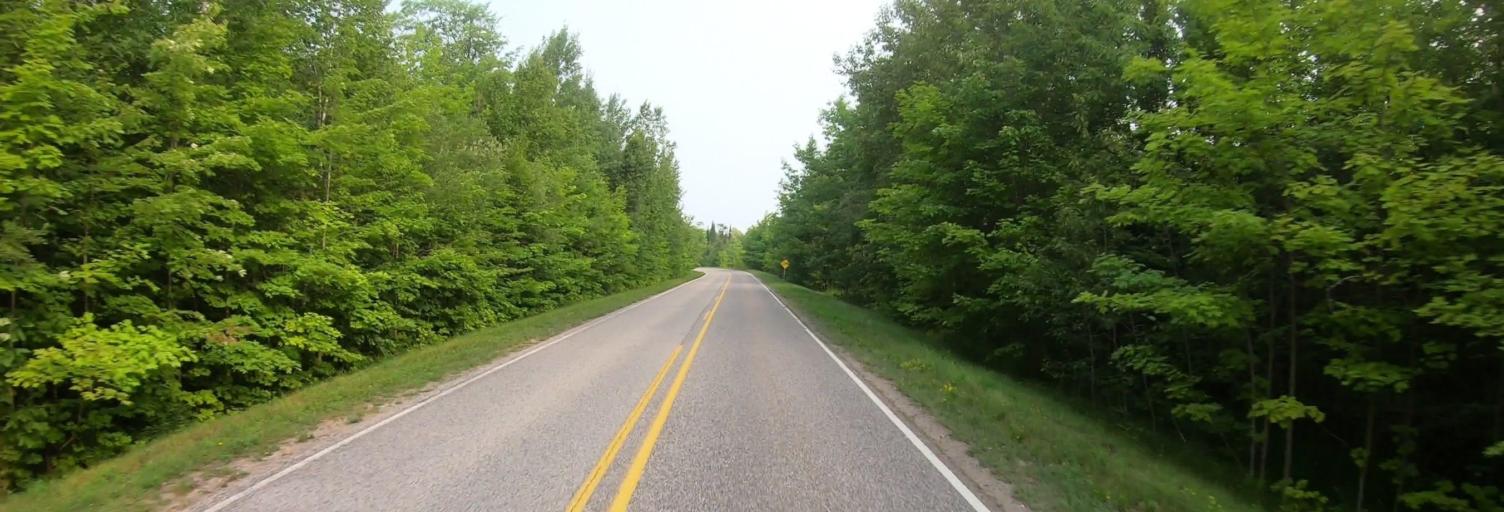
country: US
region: Michigan
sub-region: Chippewa County
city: Sault Ste. Marie
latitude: 46.4617
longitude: -84.8579
